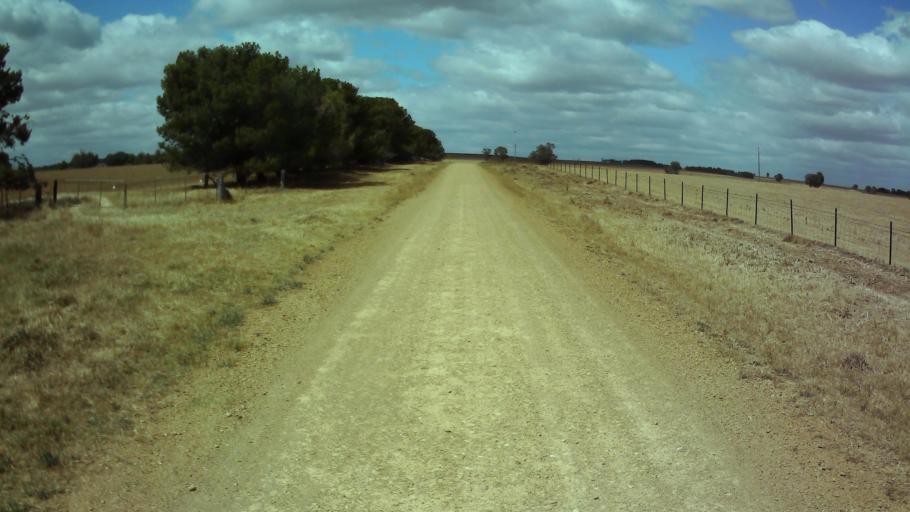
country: AU
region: New South Wales
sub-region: Weddin
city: Grenfell
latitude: -34.0637
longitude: 148.3296
